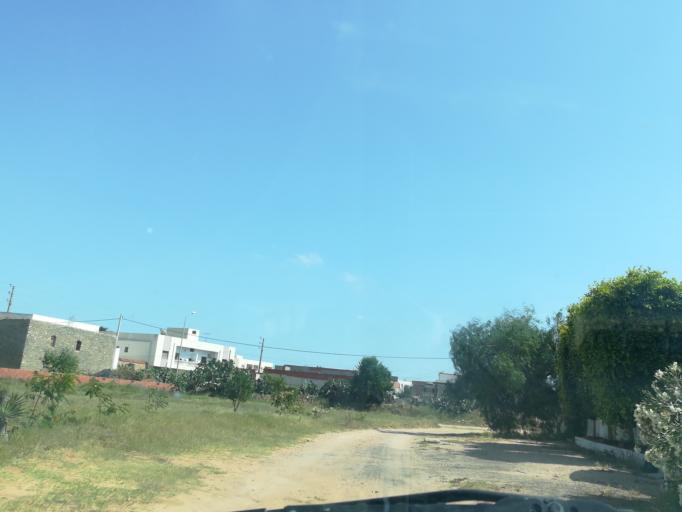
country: TN
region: Safaqis
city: Al Qarmadah
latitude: 34.8214
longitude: 10.7615
